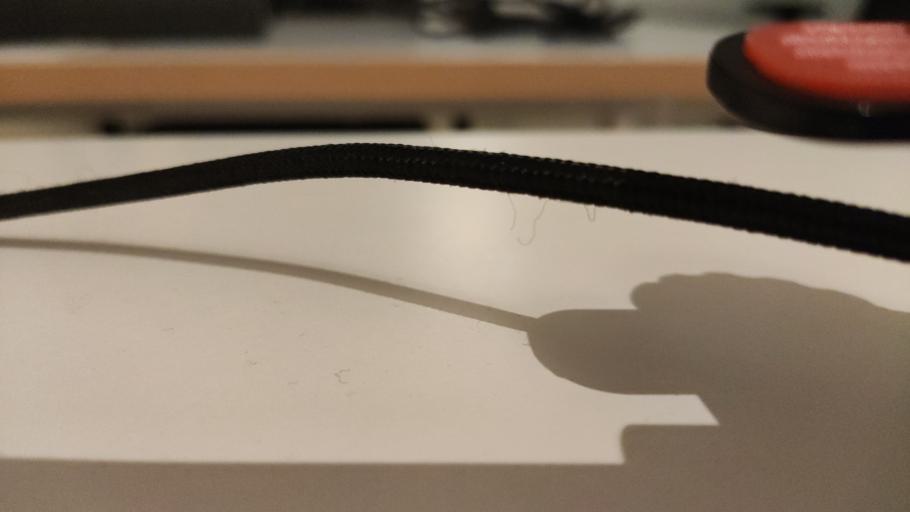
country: RU
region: Moskovskaya
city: Il'inskiy Pogost
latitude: 55.5316
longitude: 38.8725
